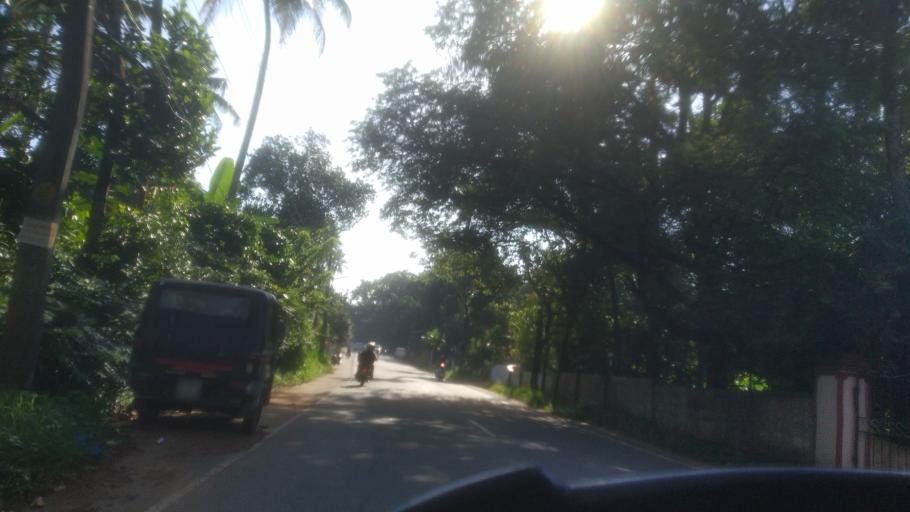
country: IN
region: Kerala
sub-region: Ernakulam
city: Muvattupuzha
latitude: 9.9800
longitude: 76.5368
